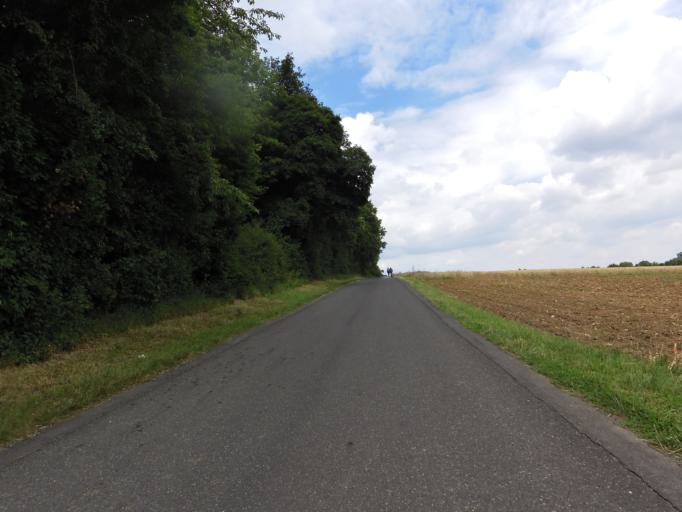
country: DE
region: Bavaria
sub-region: Regierungsbezirk Unterfranken
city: Reichenberg
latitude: 49.7600
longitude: 9.9169
